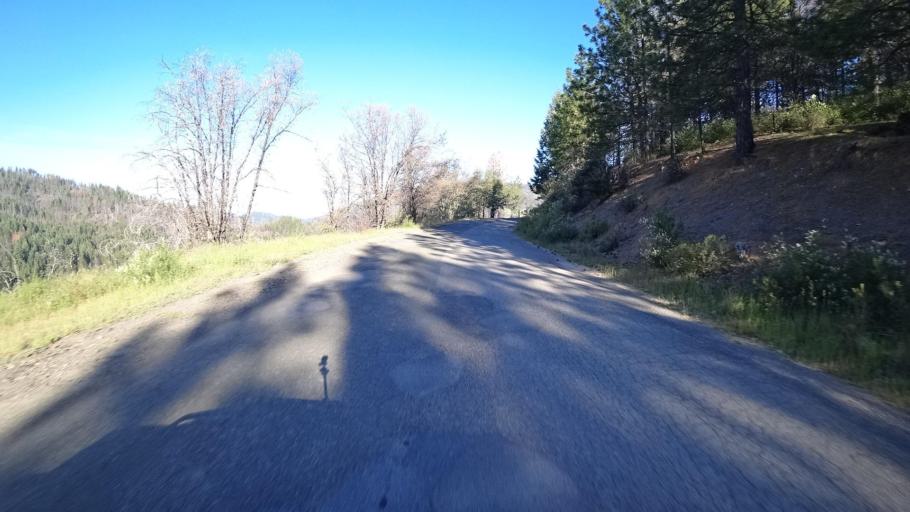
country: US
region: California
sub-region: Lake County
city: Upper Lake
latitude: 39.2925
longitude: -122.9251
